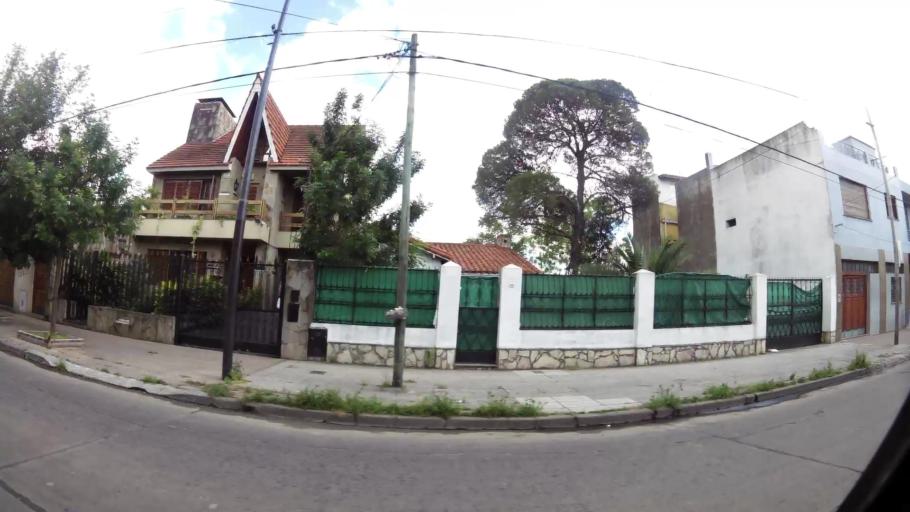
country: AR
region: Buenos Aires
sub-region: Partido de Lanus
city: Lanus
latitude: -34.6890
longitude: -58.4176
